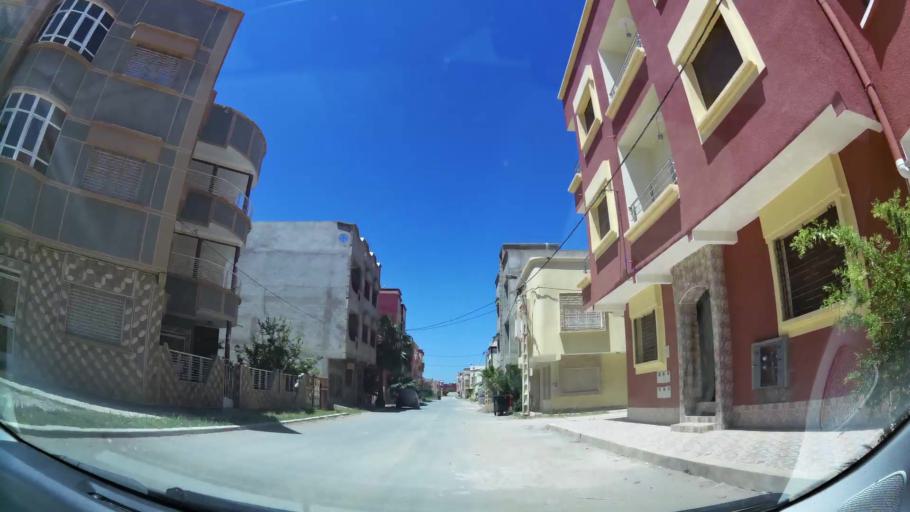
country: MA
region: Oriental
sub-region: Berkane-Taourirt
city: Madagh
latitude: 35.0804
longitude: -2.2270
